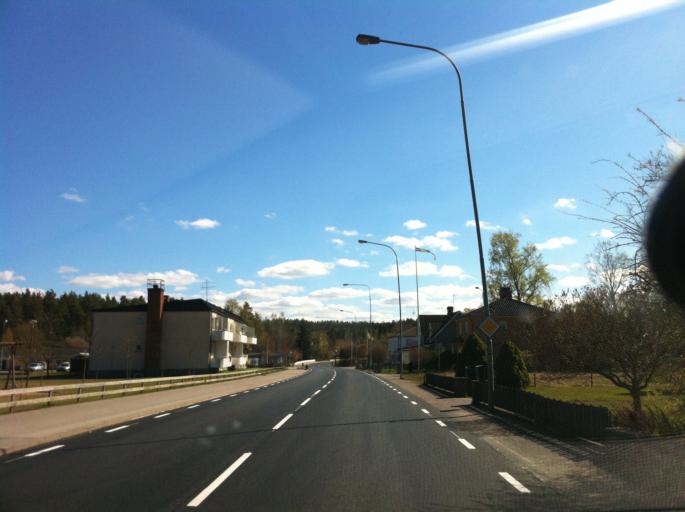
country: SE
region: Kalmar
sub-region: Hultsfreds Kommun
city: Malilla
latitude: 57.4651
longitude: 15.6602
